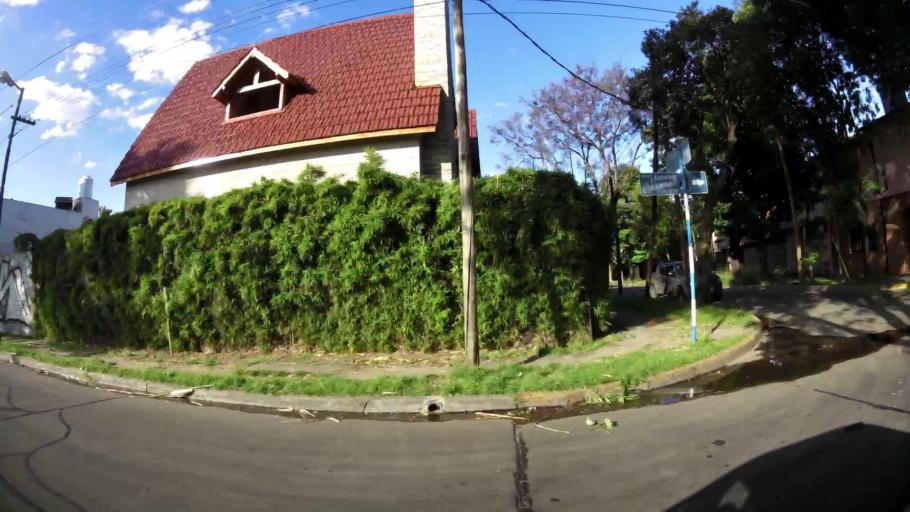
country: AR
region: Buenos Aires
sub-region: Partido de General San Martin
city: General San Martin
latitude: -34.5448
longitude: -58.5634
